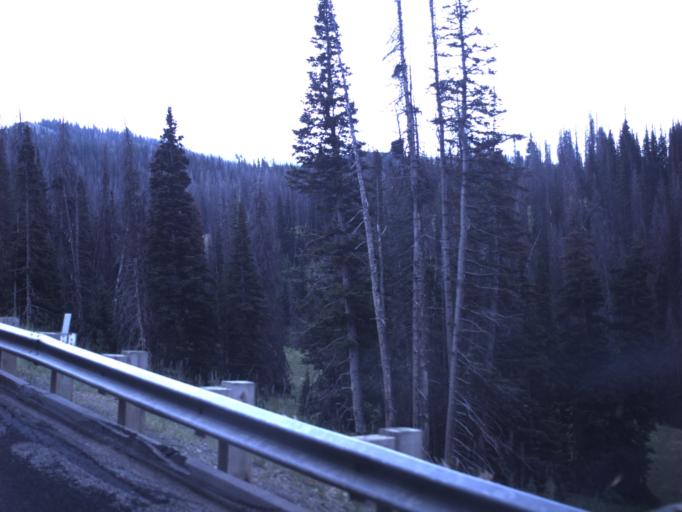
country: US
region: Utah
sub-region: Summit County
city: Francis
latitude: 40.4987
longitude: -111.0404
